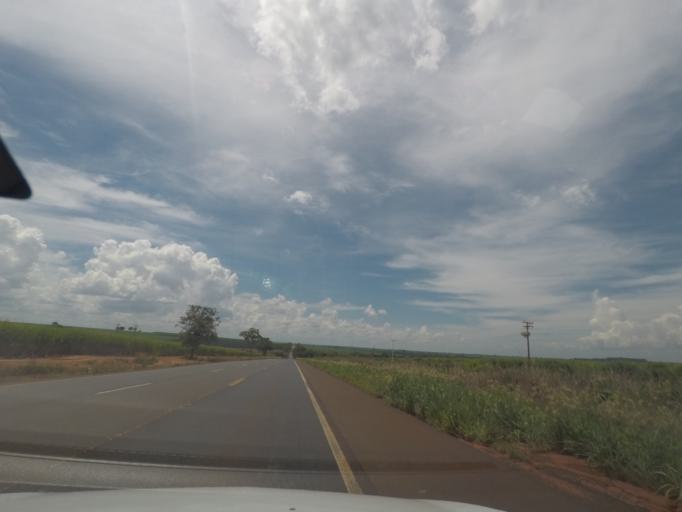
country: BR
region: Sao Paulo
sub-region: Barretos
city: Barretos
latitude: -20.2688
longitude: -48.6736
